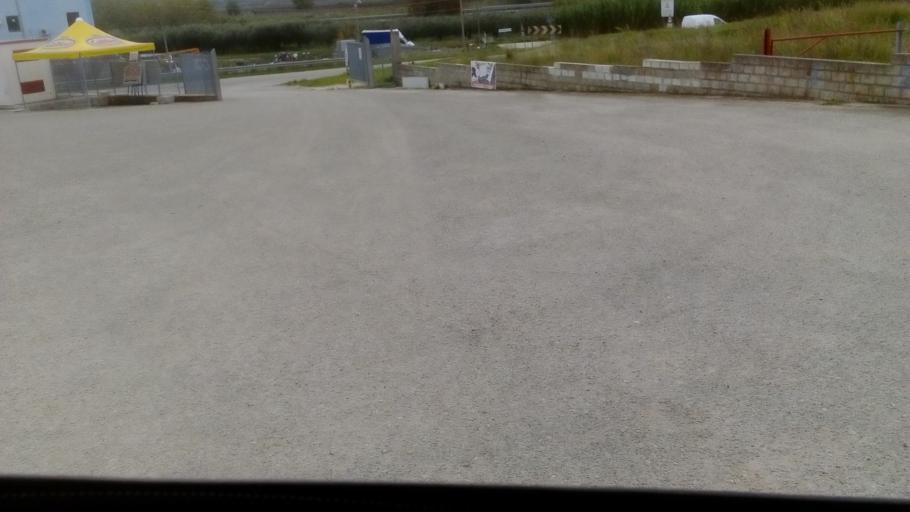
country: IT
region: Abruzzo
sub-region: Provincia di Chieti
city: San Salvo
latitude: 42.0278
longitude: 14.7372
